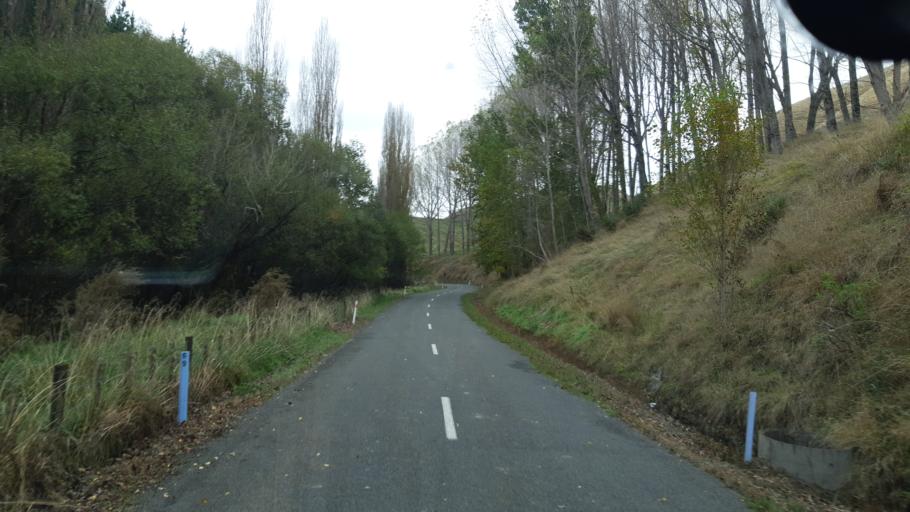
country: NZ
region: Manawatu-Wanganui
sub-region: Ruapehu District
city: Waiouru
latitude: -39.6106
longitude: 175.5826
